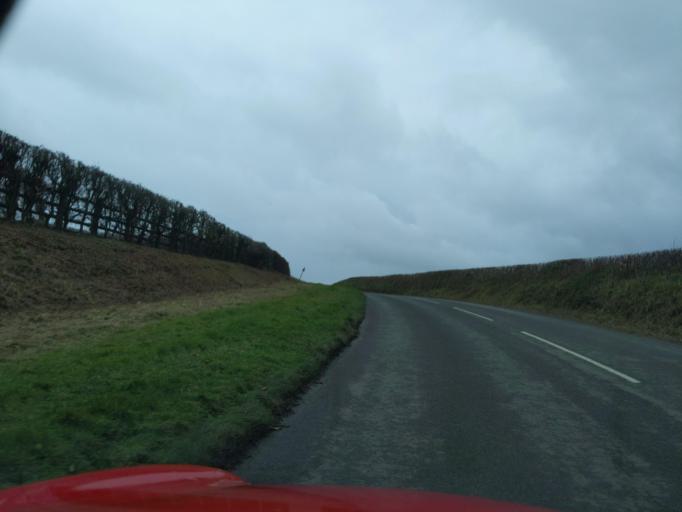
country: GB
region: England
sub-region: Devon
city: Modbury
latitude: 50.3300
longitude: -3.8777
